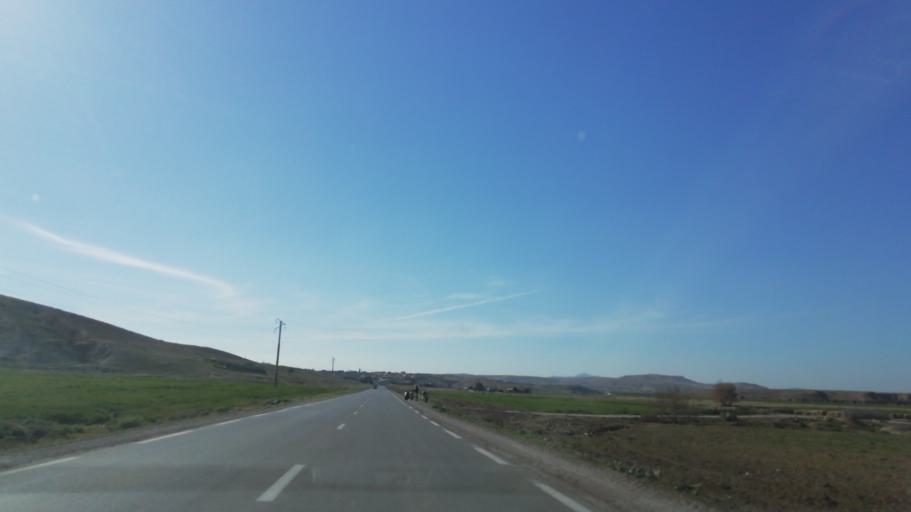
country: DZ
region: Mascara
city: Oued el Abtal
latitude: 35.4555
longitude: 0.7349
